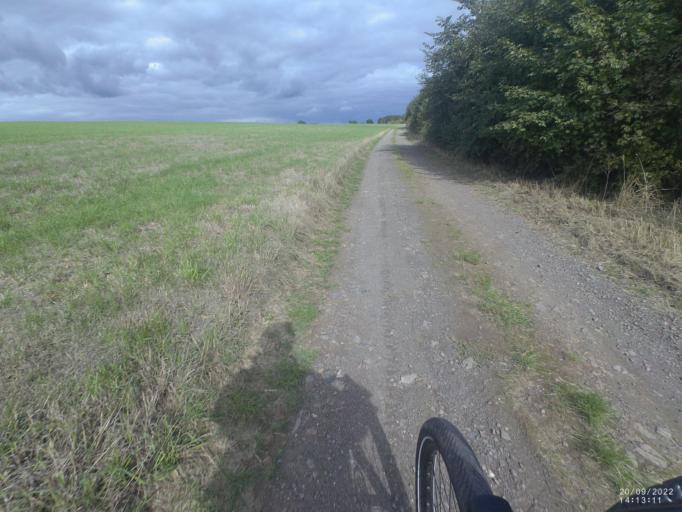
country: DE
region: Rheinland-Pfalz
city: Immerath
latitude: 50.1224
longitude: 6.9450
